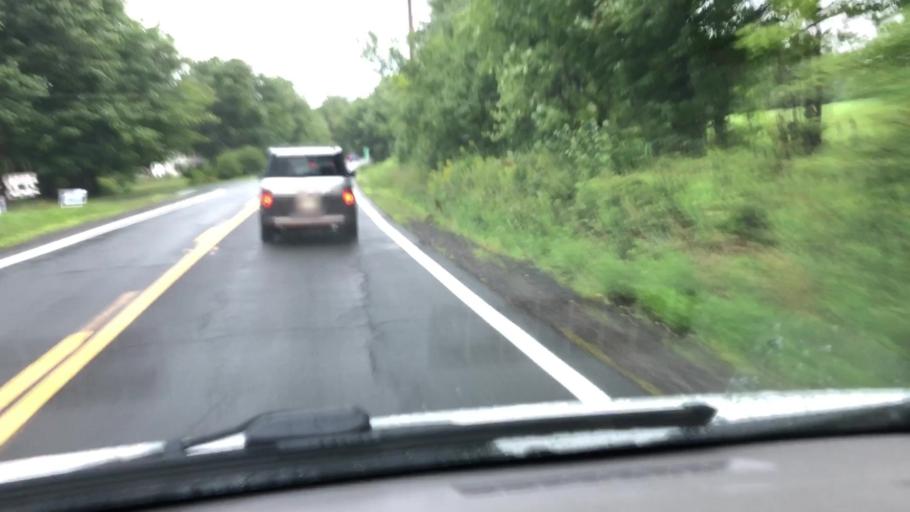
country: US
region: Massachusetts
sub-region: Hampshire County
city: Chesterfield
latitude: 42.3830
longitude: -72.9278
